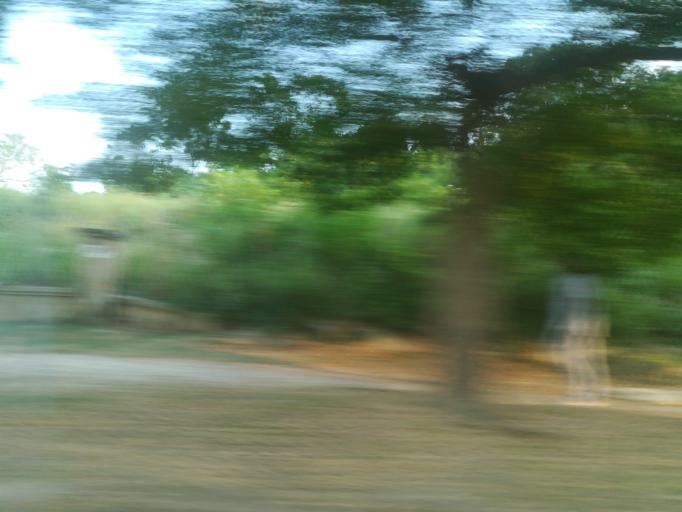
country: NG
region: Abuja Federal Capital Territory
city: Abuja
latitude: 9.0684
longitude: 7.4122
